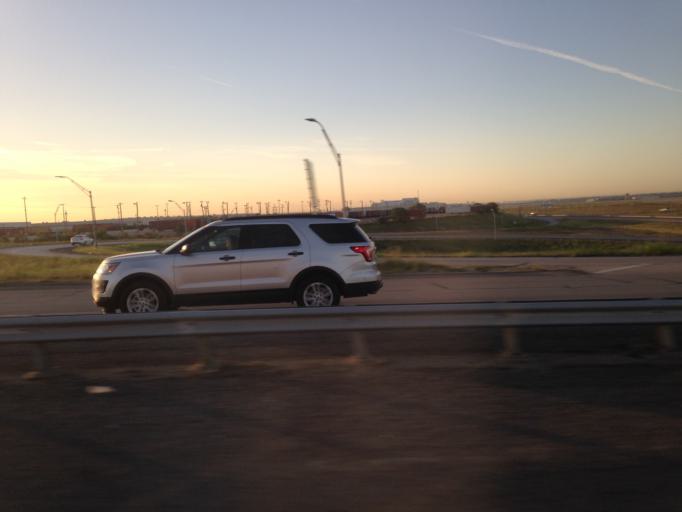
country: US
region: Texas
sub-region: Tarrant County
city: Saginaw
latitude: 32.8364
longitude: -97.3631
